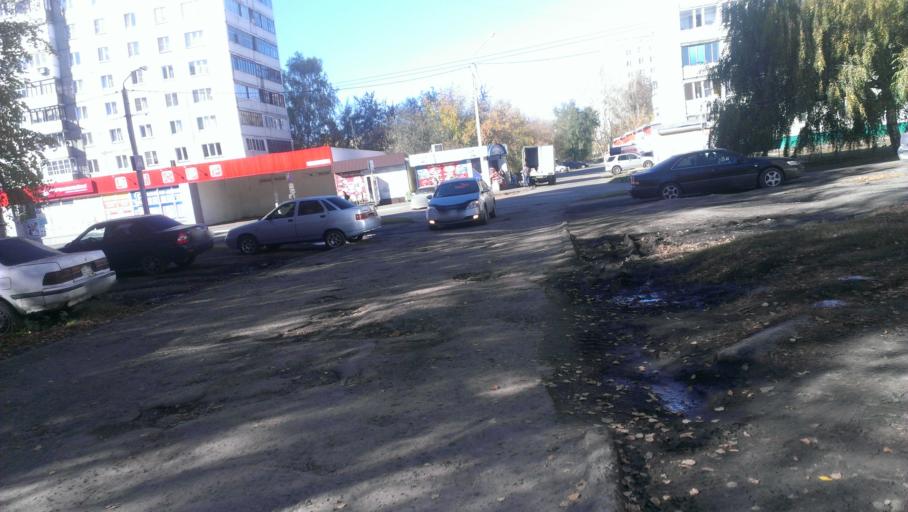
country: RU
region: Altai Krai
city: Novosilikatnyy
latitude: 53.3662
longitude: 83.6690
